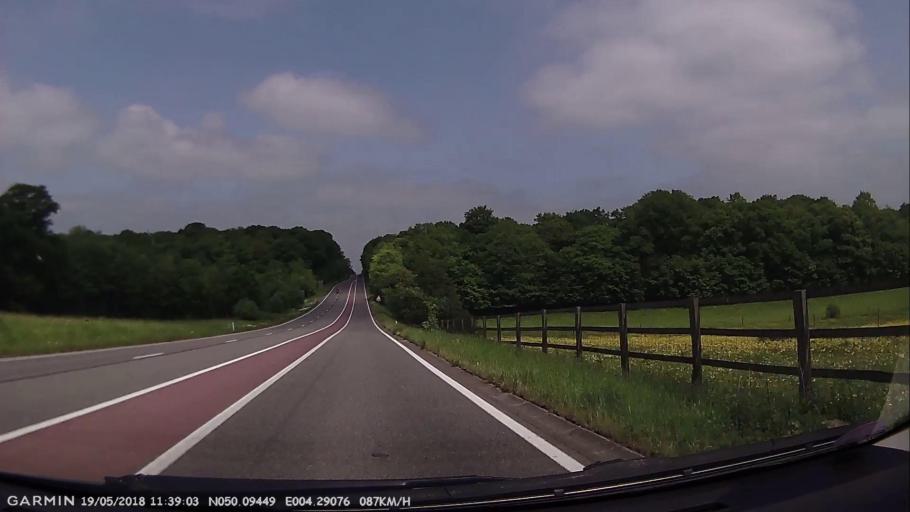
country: BE
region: Wallonia
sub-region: Province du Hainaut
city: Chimay
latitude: 50.0948
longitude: 4.2907
